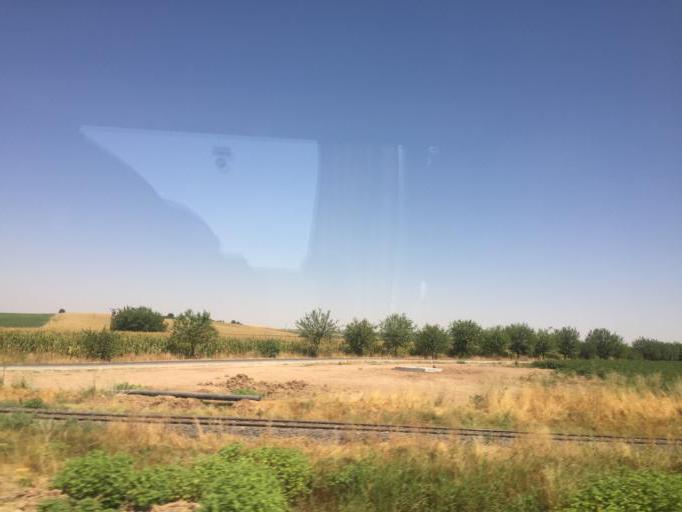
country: TR
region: Diyarbakir
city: Tepe
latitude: 37.8508
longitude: 40.7520
